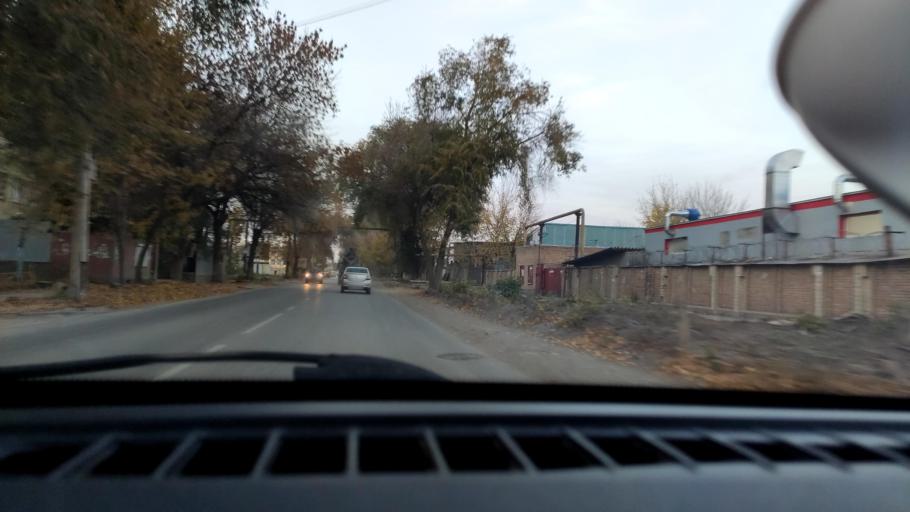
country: RU
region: Samara
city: Samara
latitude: 53.1889
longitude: 50.2450
